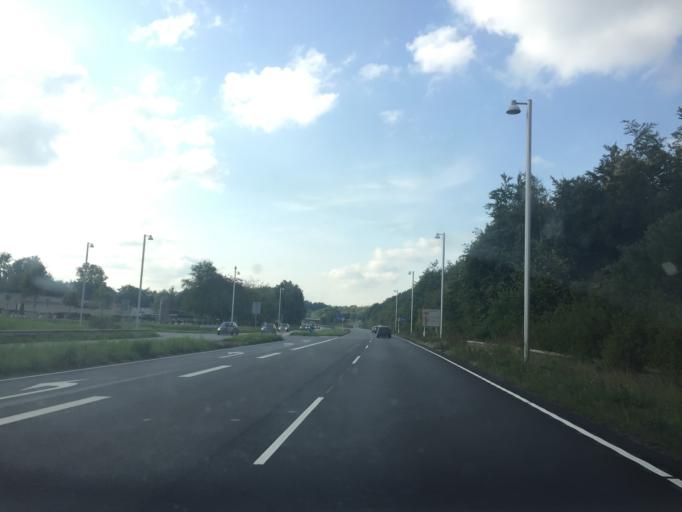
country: DK
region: Zealand
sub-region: Holbaek Kommune
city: Jyderup
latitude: 55.6611
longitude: 11.4168
